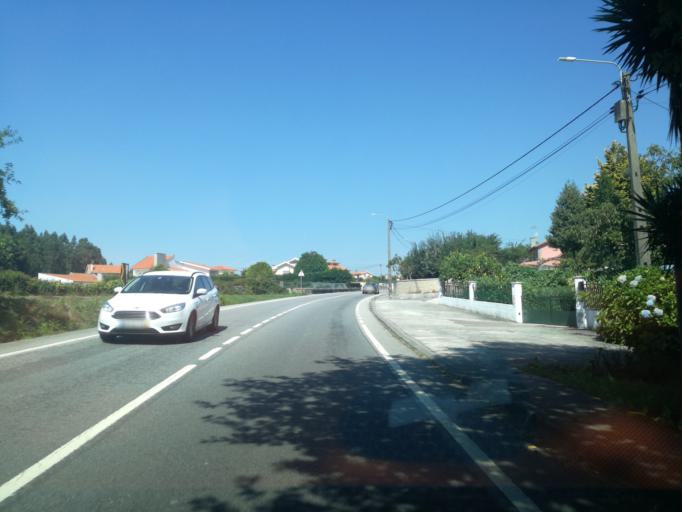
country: PT
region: Braga
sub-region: Esposende
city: Marinhas
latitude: 41.6202
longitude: -8.7770
